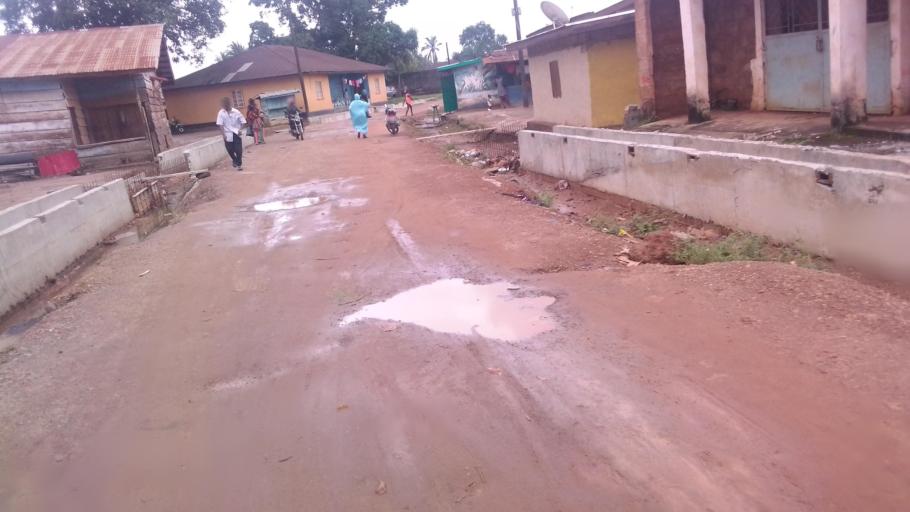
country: SL
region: Eastern Province
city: Kenema
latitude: 7.8860
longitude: -11.1845
